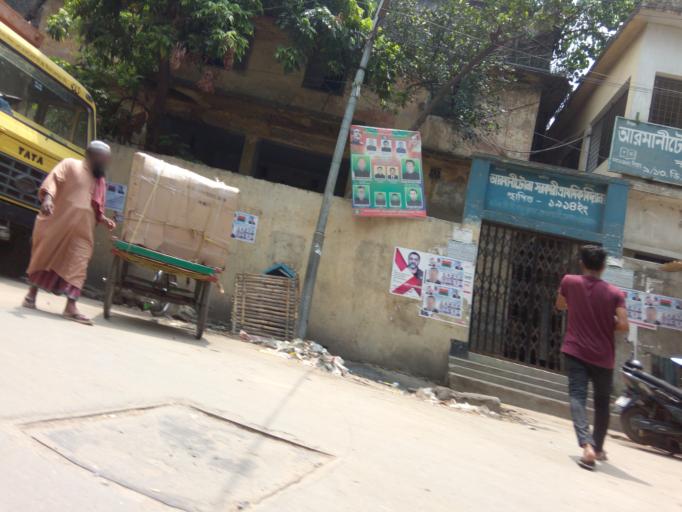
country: BD
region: Dhaka
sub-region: Dhaka
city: Dhaka
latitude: 23.7137
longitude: 90.4012
